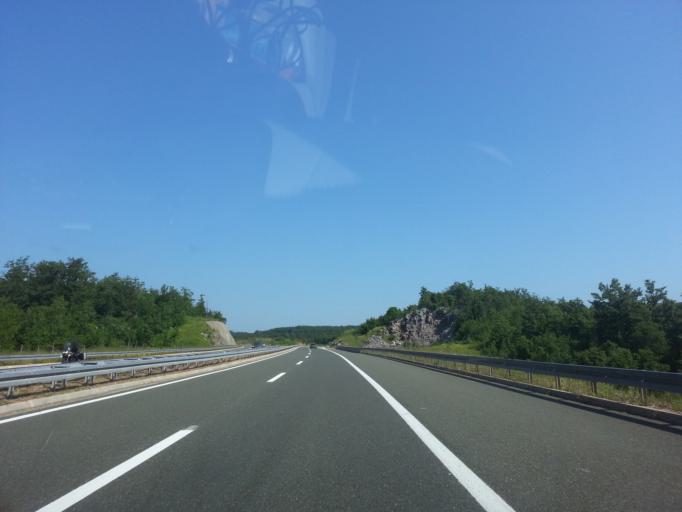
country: HR
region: Primorsko-Goranska
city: Matulji
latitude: 45.4204
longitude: 14.3004
